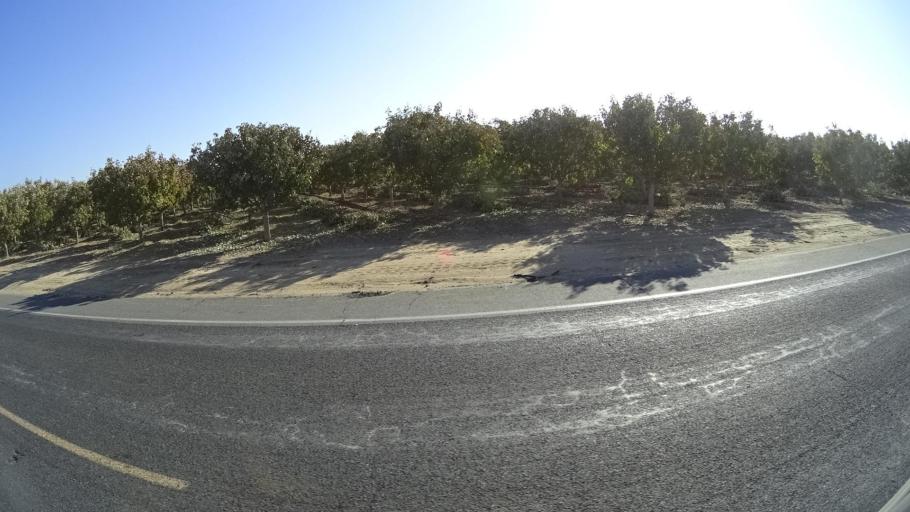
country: US
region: California
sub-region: Tulare County
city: Richgrove
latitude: 35.7497
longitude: -119.1401
